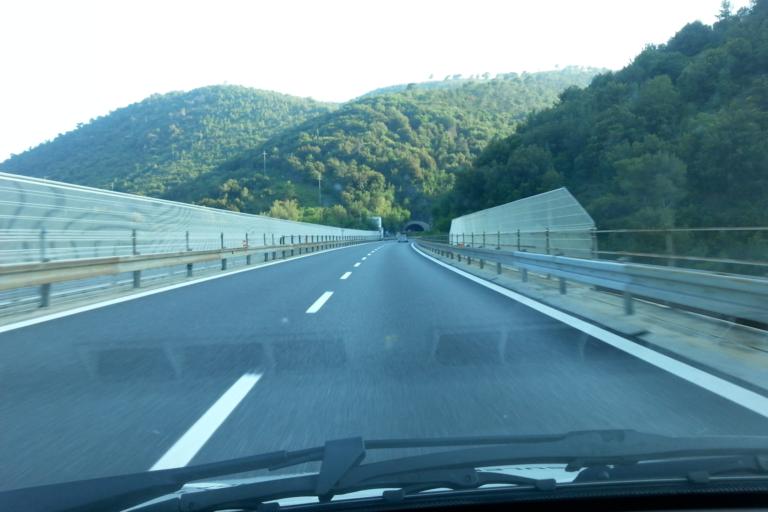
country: IT
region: Liguria
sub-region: Provincia di Savona
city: Borgio
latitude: 44.1755
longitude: 8.2944
